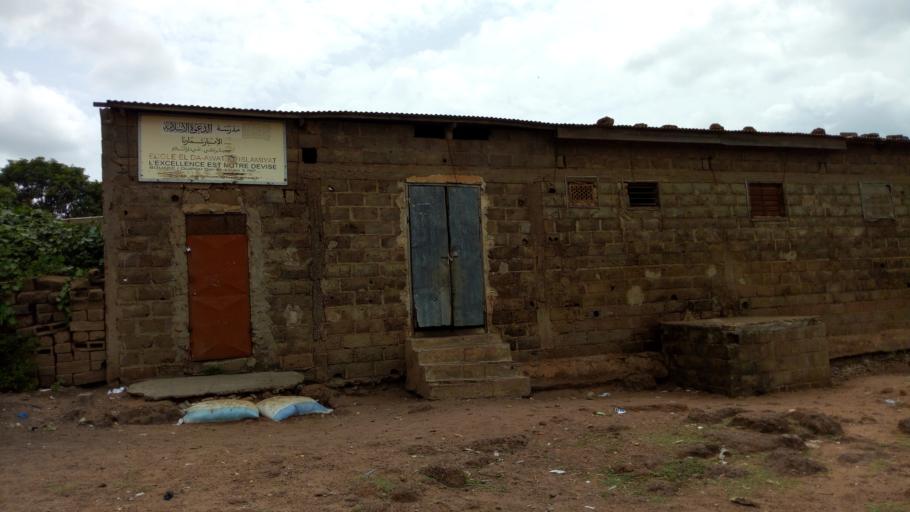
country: CI
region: Vallee du Bandama
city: Bouake
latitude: 7.7253
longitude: -5.0221
